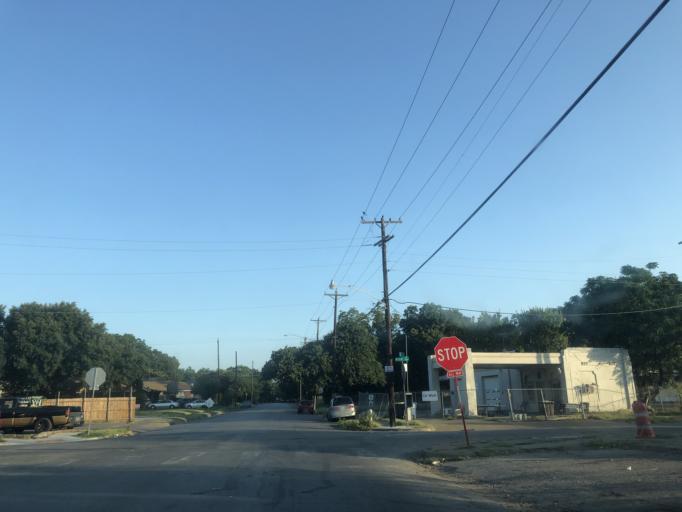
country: US
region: Texas
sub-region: Dallas County
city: Dallas
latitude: 32.7521
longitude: -96.7662
